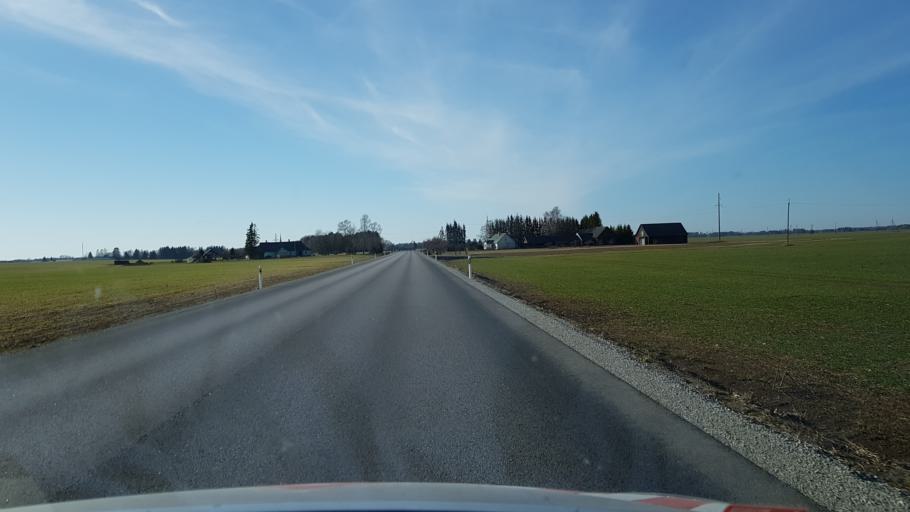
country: EE
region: Laeaene-Virumaa
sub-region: Vinni vald
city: Vinni
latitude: 59.2371
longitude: 26.4953
